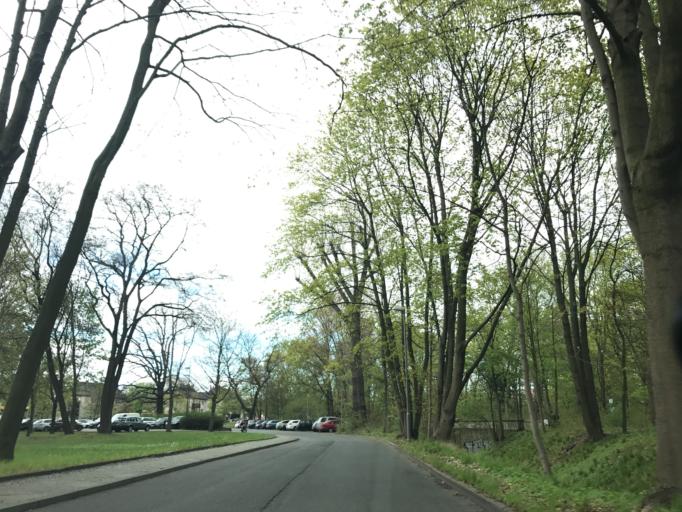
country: DE
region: Berlin
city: Reinickendorf
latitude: 52.5593
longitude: 13.3258
